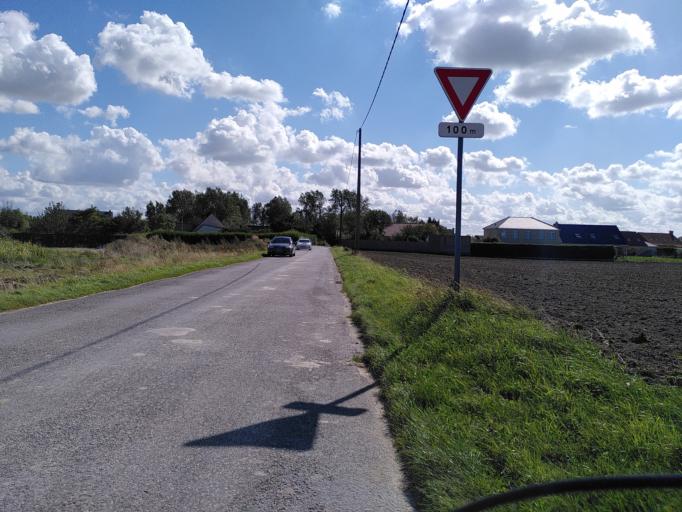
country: FR
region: Nord-Pas-de-Calais
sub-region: Departement du Pas-de-Calais
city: Oye-Plage
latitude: 50.9889
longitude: 2.0397
